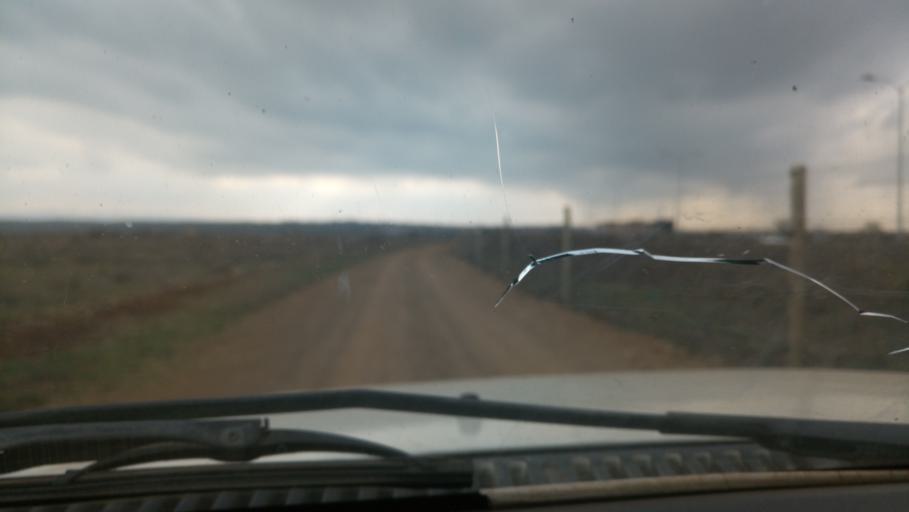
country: KE
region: Nairobi Area
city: Nairobi
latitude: -1.3331
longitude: 36.8234
